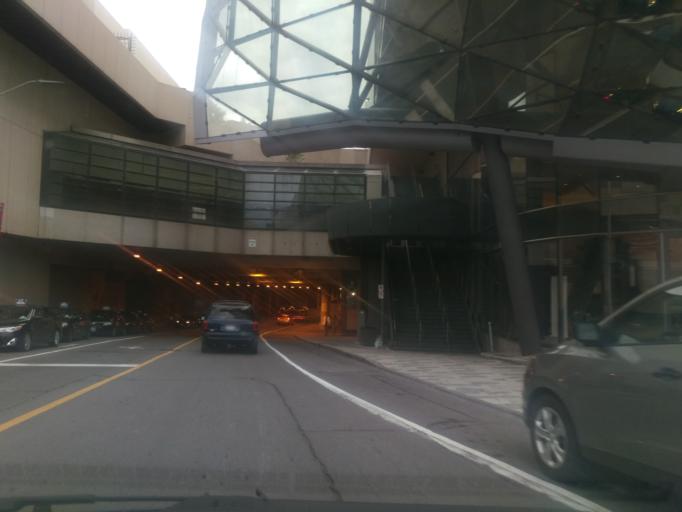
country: CA
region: Ontario
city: Ottawa
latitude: 45.4243
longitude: -75.6921
